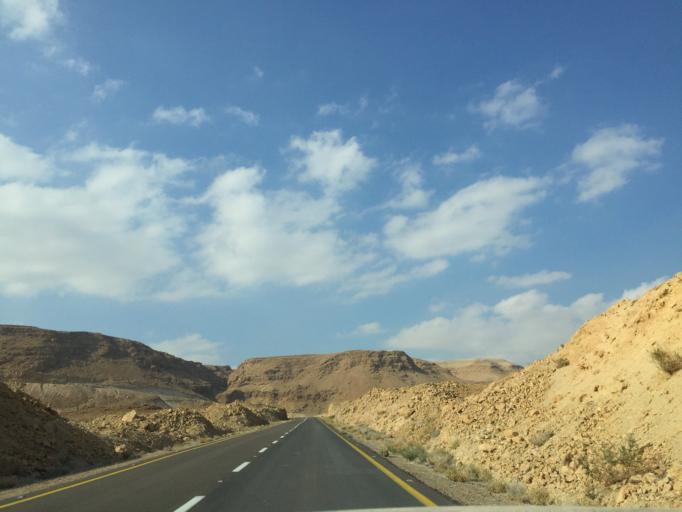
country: IL
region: Southern District
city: `En Boqeq
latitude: 31.3203
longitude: 35.3403
